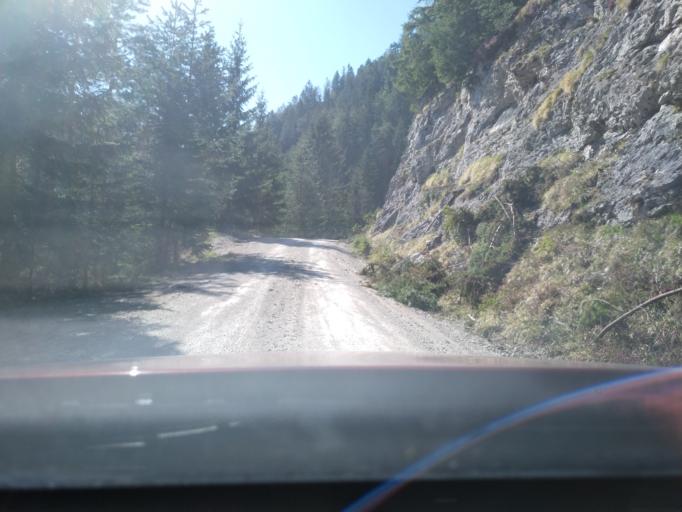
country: AT
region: Lower Austria
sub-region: Politischer Bezirk Wiener Neustadt
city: Gutenstein
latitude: 47.8229
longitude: 15.8423
